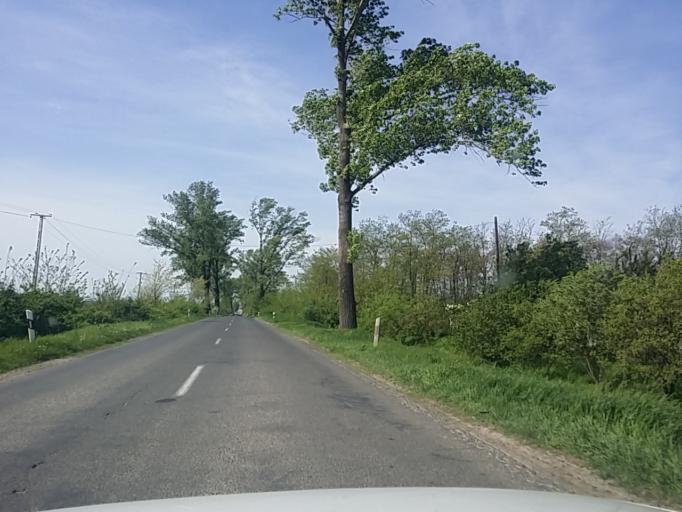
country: HU
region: Bekes
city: Doboz
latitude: 46.7144
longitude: 21.1869
